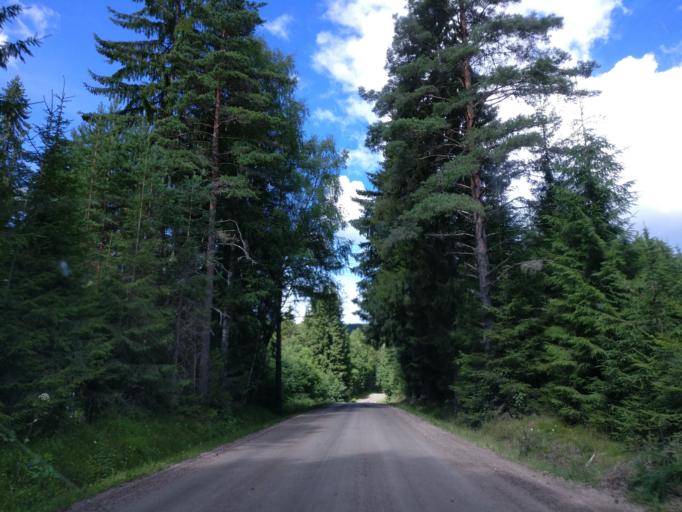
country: SE
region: Vaermland
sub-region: Hagfors Kommun
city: Ekshaerad
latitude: 60.0522
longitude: 13.4819
